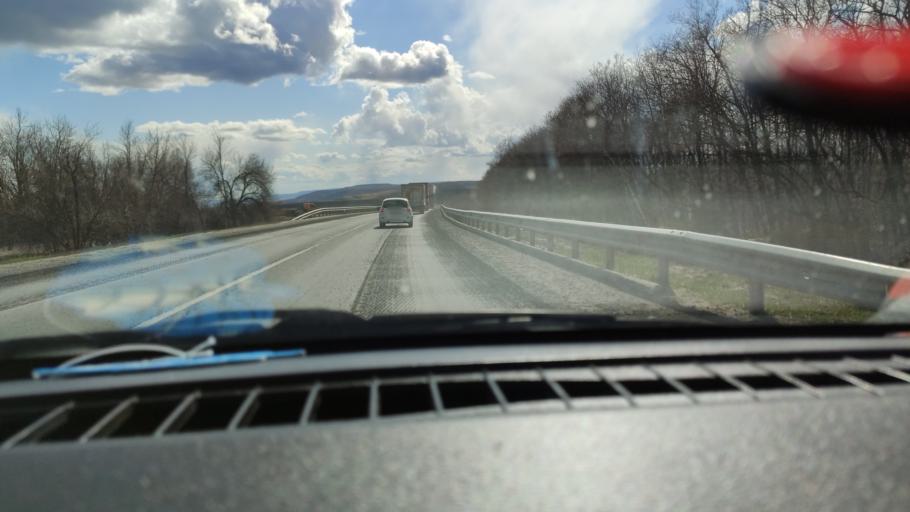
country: RU
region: Saratov
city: Dukhovnitskoye
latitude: 52.7074
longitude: 48.2618
